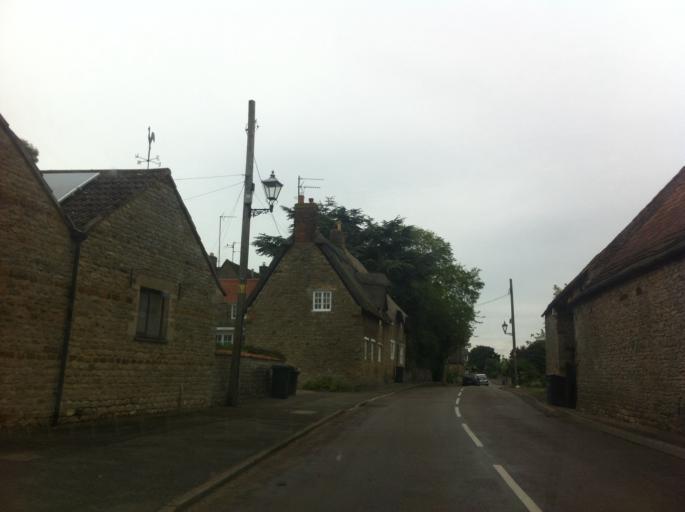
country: GB
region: England
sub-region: Northamptonshire
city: Wellingborough
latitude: 52.2745
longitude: -0.7069
